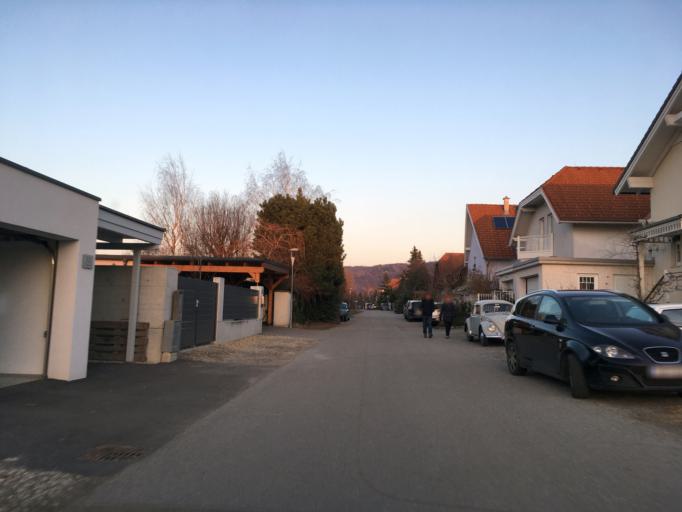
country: AT
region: Lower Austria
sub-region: Politischer Bezirk Tulln
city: Wordern
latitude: 48.3245
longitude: 16.2038
